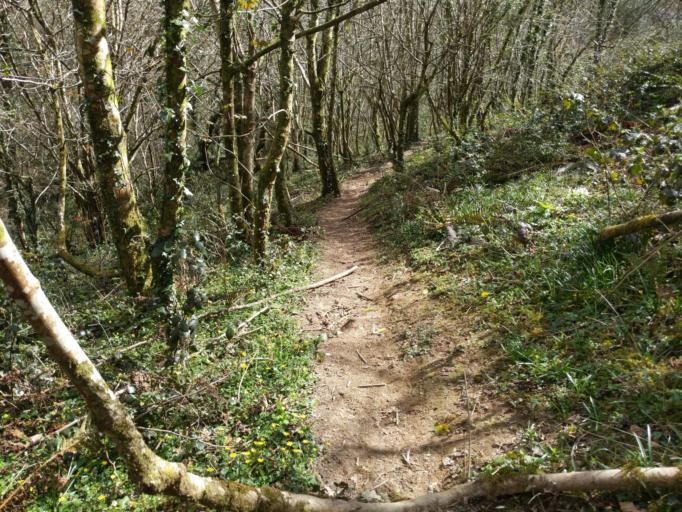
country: GB
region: England
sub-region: Plymouth
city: Plymouth
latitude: 50.4222
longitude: -4.1492
